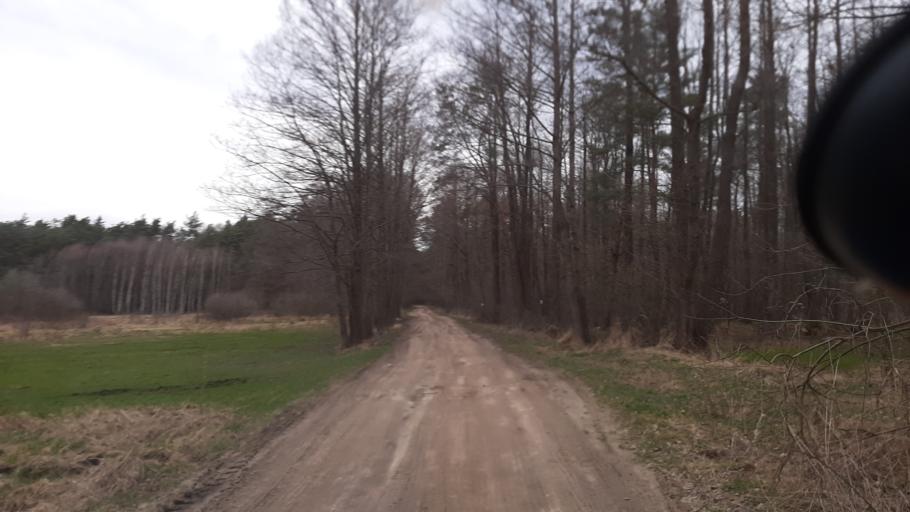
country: PL
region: Lublin Voivodeship
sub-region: Powiat lubartowski
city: Abramow
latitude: 51.4411
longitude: 22.3454
